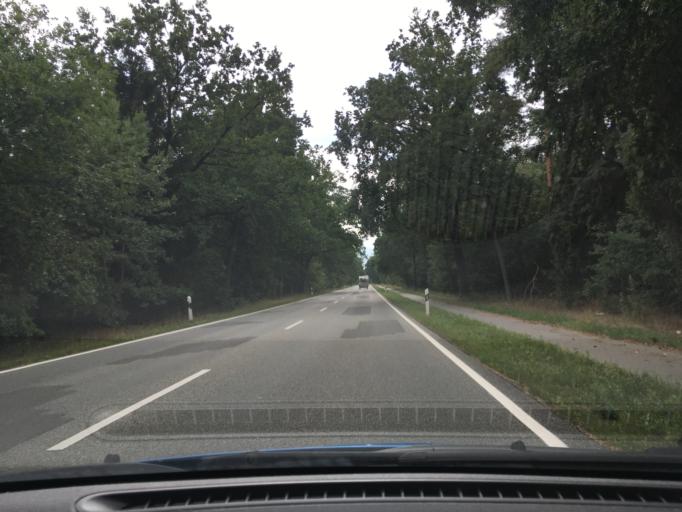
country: DE
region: Mecklenburg-Vorpommern
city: Stralendorf
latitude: 53.5517
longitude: 11.3277
